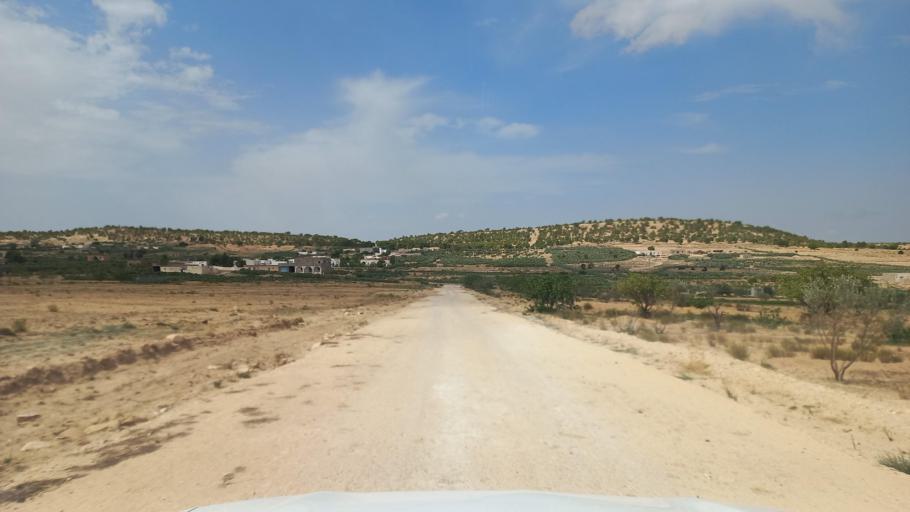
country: TN
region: Al Qasrayn
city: Kasserine
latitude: 35.3865
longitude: 8.8641
